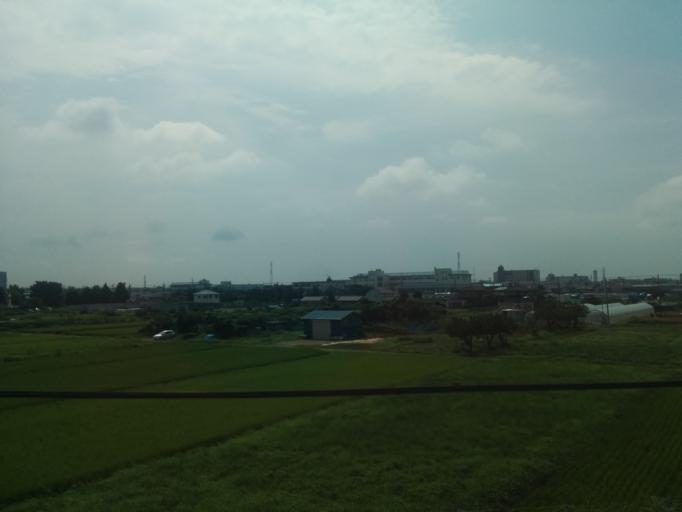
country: JP
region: Kanagawa
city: Isehara
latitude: 35.3817
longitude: 139.3567
